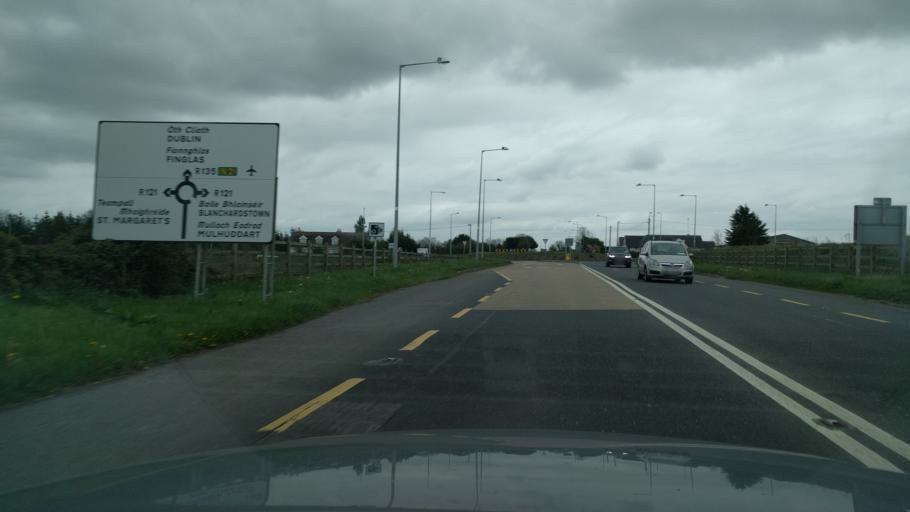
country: IE
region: Leinster
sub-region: Fingal County
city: Blanchardstown
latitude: 53.4462
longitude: -6.3423
